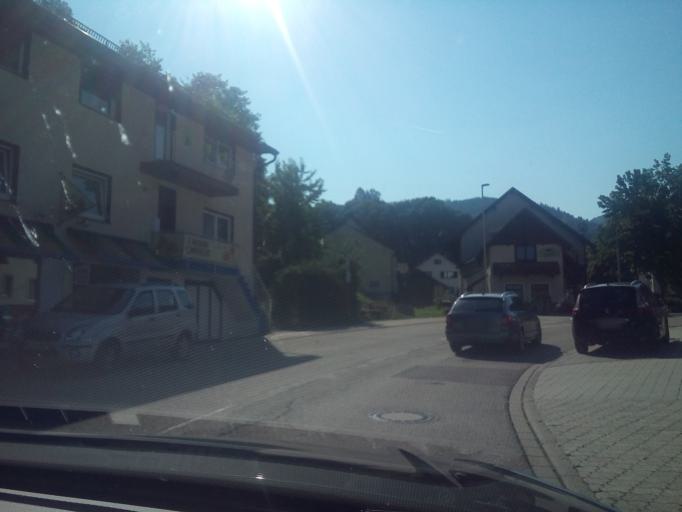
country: DE
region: Baden-Wuerttemberg
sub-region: Karlsruhe Region
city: Buhlertal
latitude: 48.6835
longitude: 8.1912
